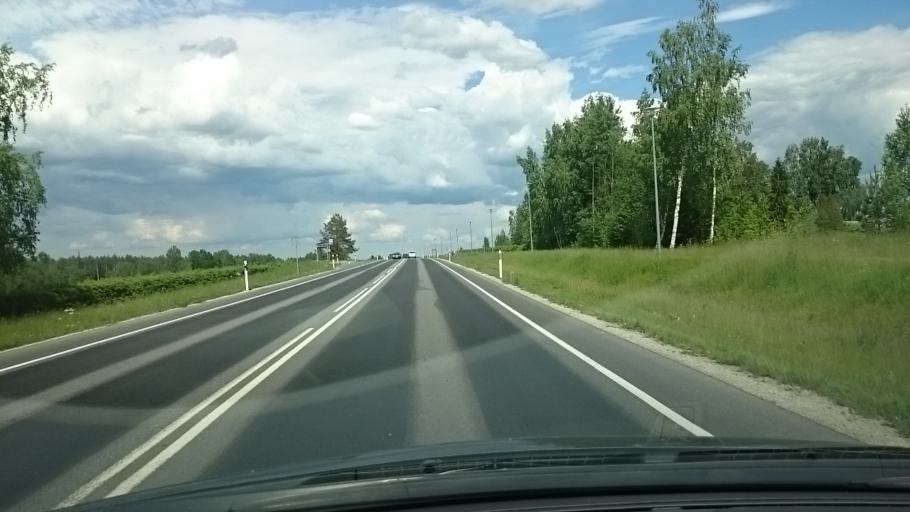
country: EE
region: Jaervamaa
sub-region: Tueri vald
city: Tueri
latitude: 58.8369
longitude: 25.4726
